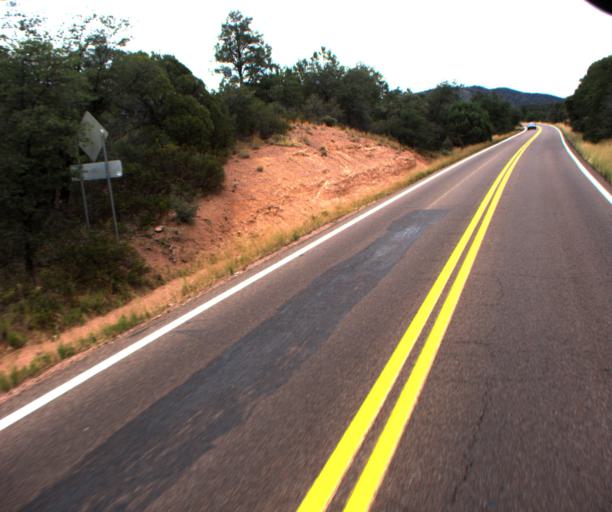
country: US
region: Arizona
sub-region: Gila County
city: Star Valley
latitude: 34.2621
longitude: -111.2119
